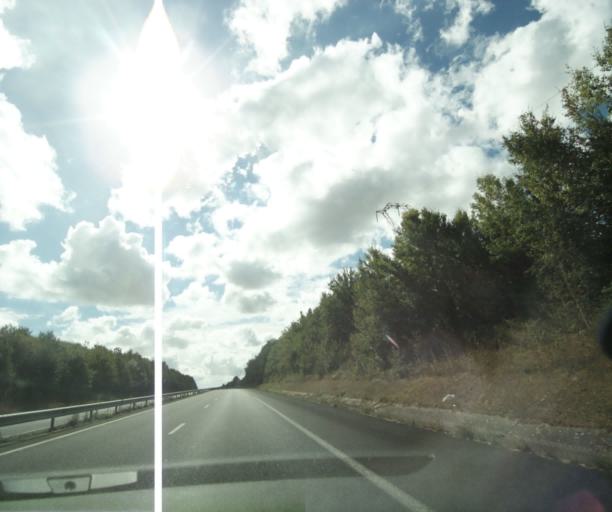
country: FR
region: Poitou-Charentes
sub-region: Departement de la Charente-Maritime
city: Saint-Georges-des-Coteaux
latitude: 45.8192
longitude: -0.7050
